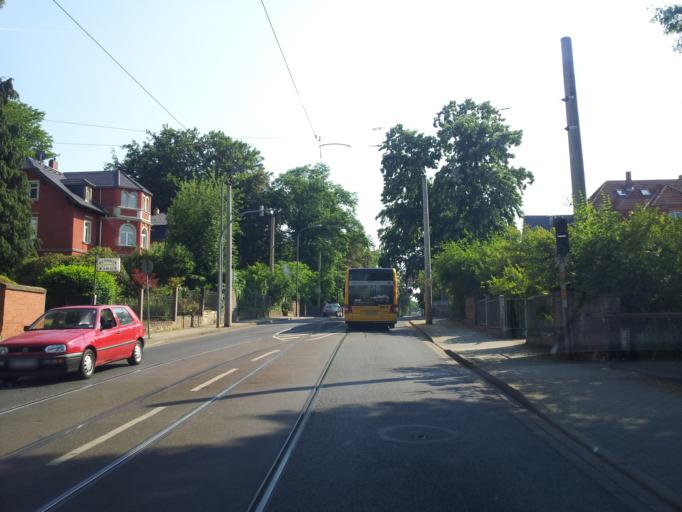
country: DE
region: Saxony
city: Albertstadt
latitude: 51.1183
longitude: 13.7893
